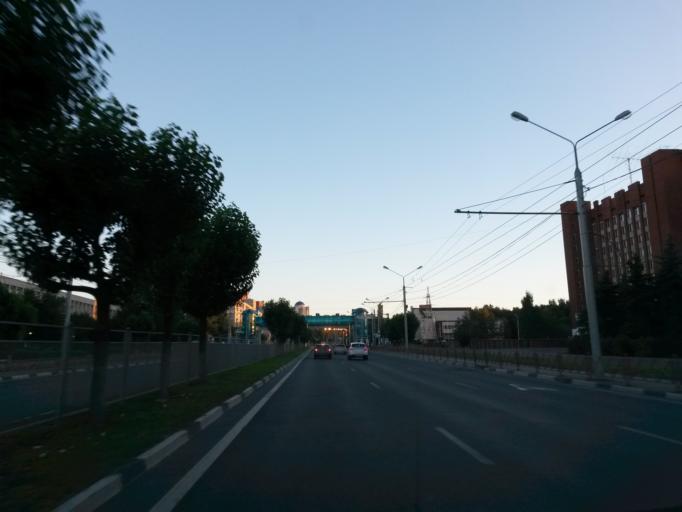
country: RU
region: Jaroslavl
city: Yaroslavl
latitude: 57.5873
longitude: 39.8575
